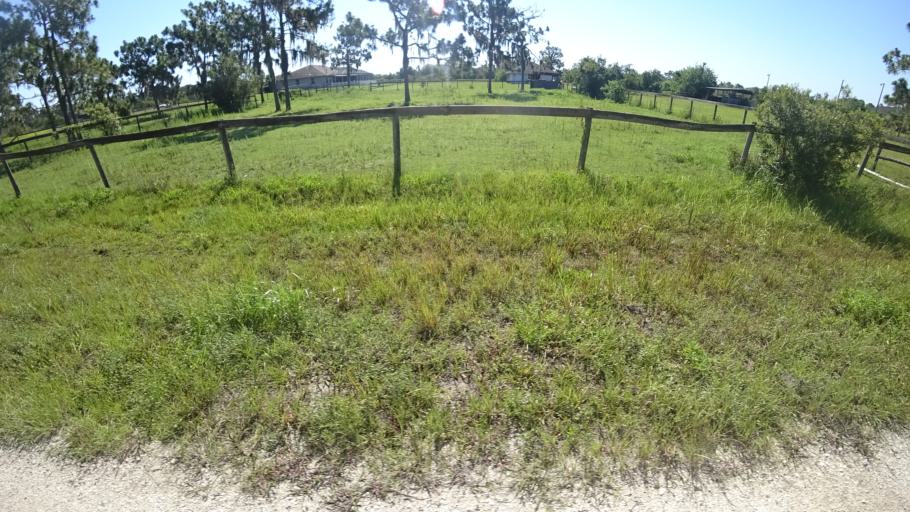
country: US
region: Florida
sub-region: Sarasota County
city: Fruitville
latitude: 27.4006
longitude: -82.2958
